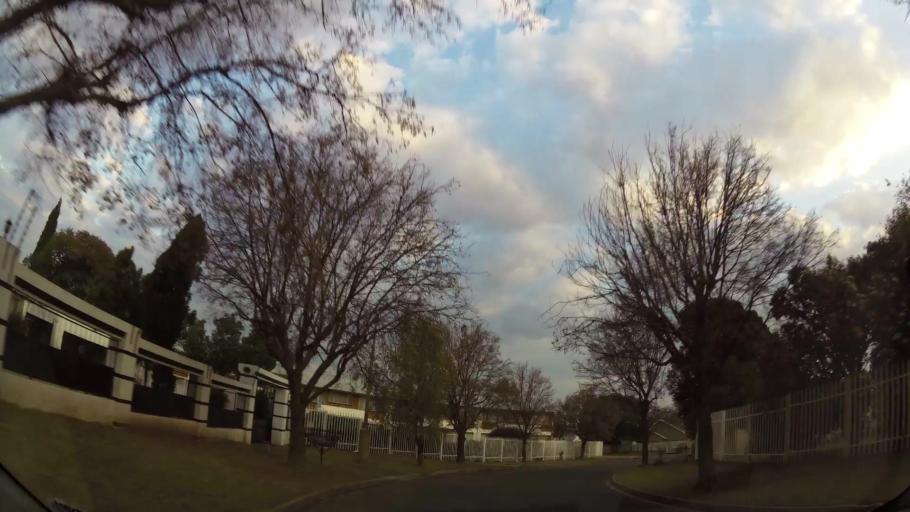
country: ZA
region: Gauteng
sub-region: Ekurhuleni Metropolitan Municipality
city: Benoni
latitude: -26.1751
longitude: 28.2999
